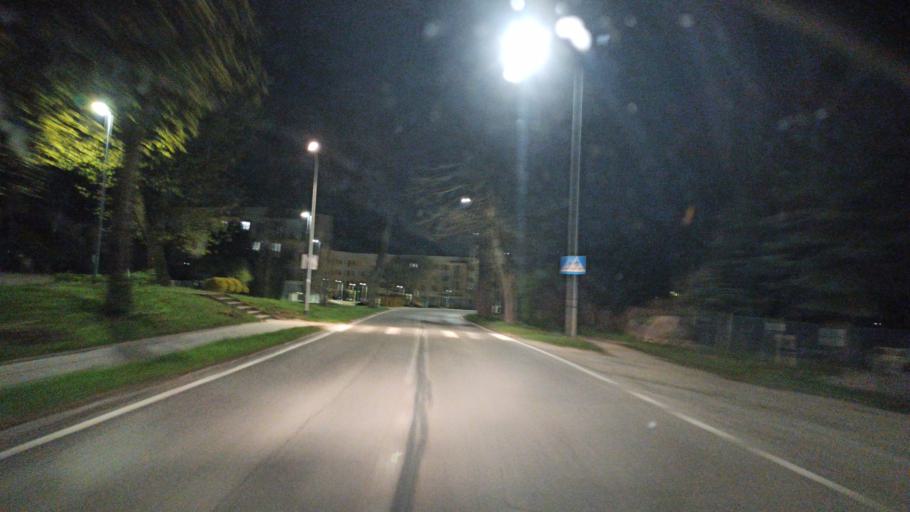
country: PL
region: Warmian-Masurian Voivodeship
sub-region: Powiat elblaski
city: Gronowo Gorne
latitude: 54.1572
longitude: 19.4460
